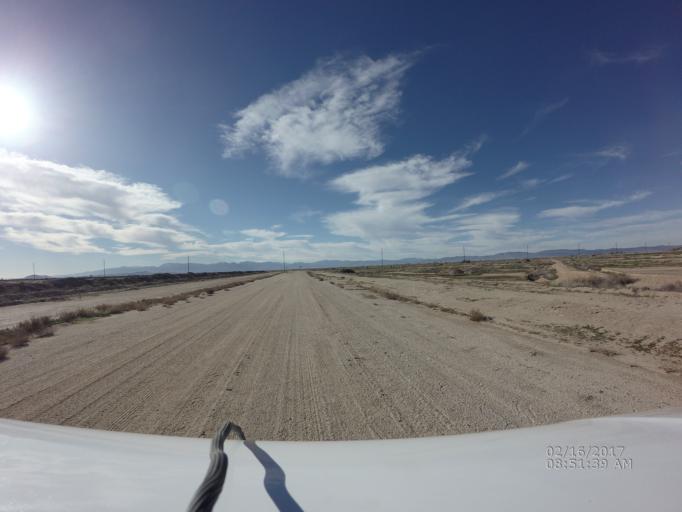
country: US
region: California
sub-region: Kern County
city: Edwards Air Force Base
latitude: 34.7657
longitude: -117.9875
